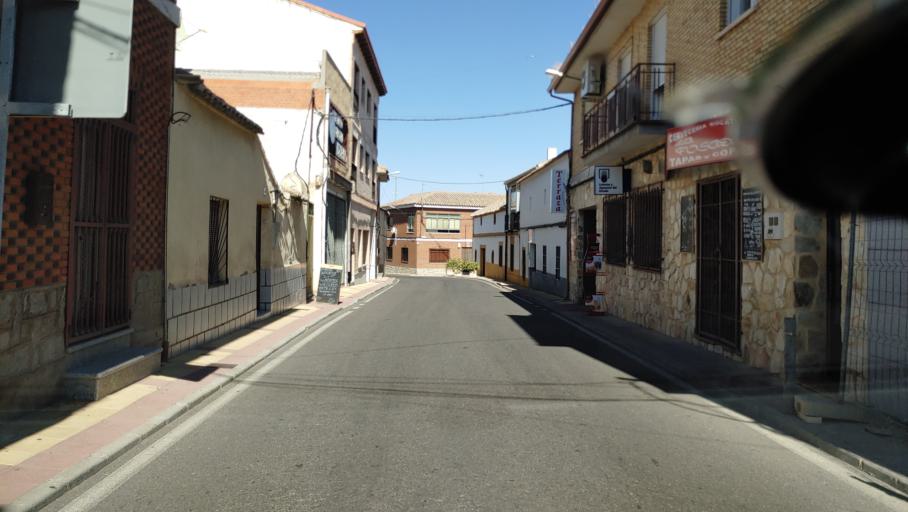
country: ES
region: Castille-La Mancha
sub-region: Province of Toledo
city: Pulgar
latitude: 39.6948
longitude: -4.1527
